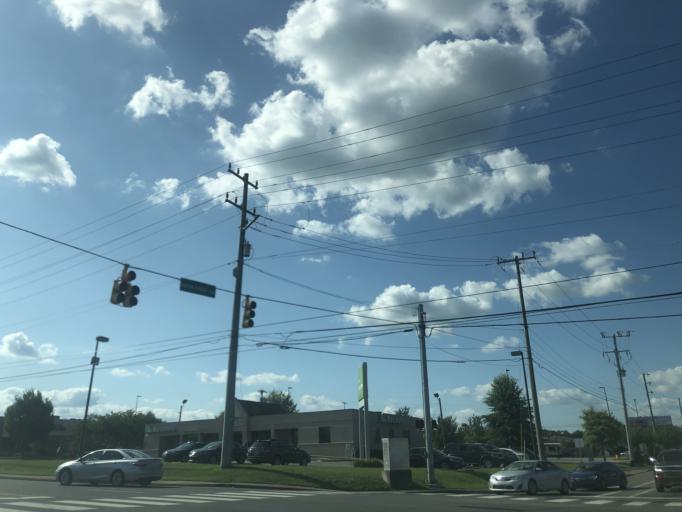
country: US
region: Tennessee
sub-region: Davidson County
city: Lakewood
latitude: 36.2151
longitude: -86.5977
